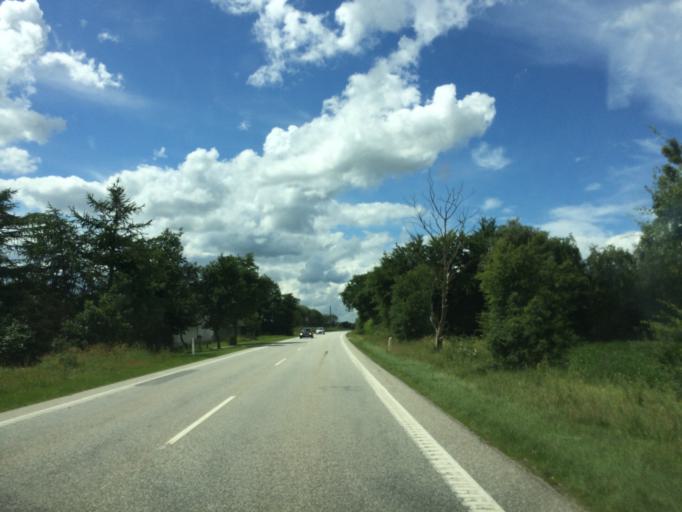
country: DK
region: North Denmark
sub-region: Vesthimmerland Kommune
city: Alestrup
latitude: 56.6210
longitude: 9.5224
